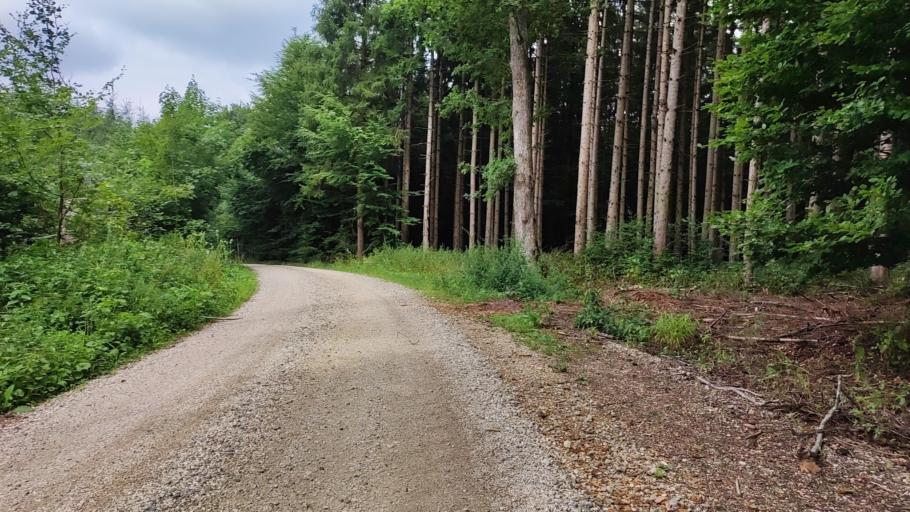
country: DE
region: Bavaria
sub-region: Swabia
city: Jettingen-Scheppach
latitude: 48.3786
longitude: 10.3937
